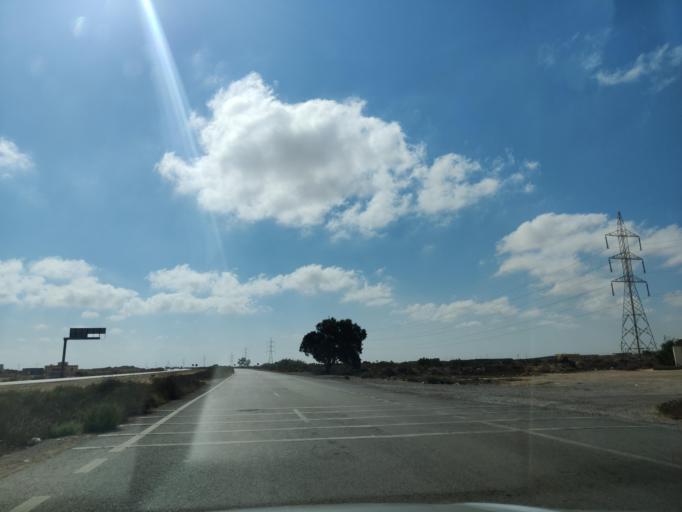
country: EG
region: Muhafazat Matruh
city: Al `Alamayn
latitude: 31.0548
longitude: 28.2602
